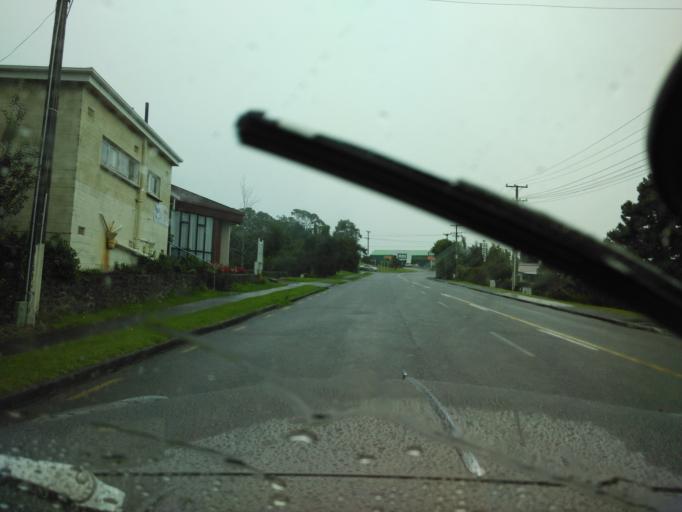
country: NZ
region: Auckland
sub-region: Auckland
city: Wellsford
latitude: -36.2976
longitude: 174.5221
